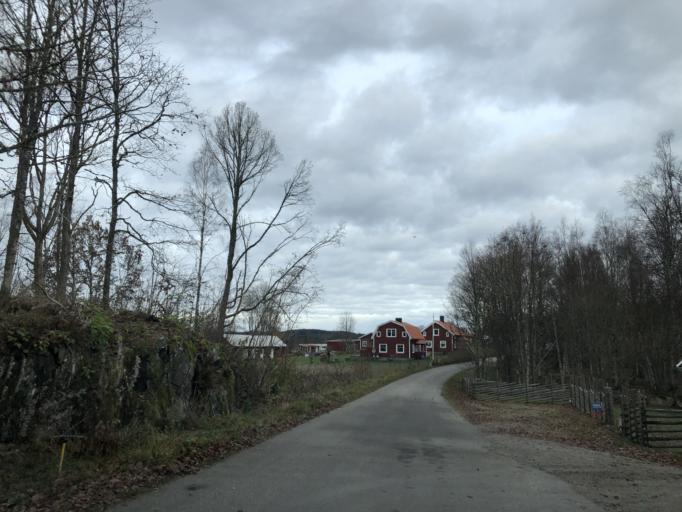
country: SE
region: Vaestra Goetaland
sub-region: Ulricehamns Kommun
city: Ulricehamn
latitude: 57.7170
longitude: 13.3585
